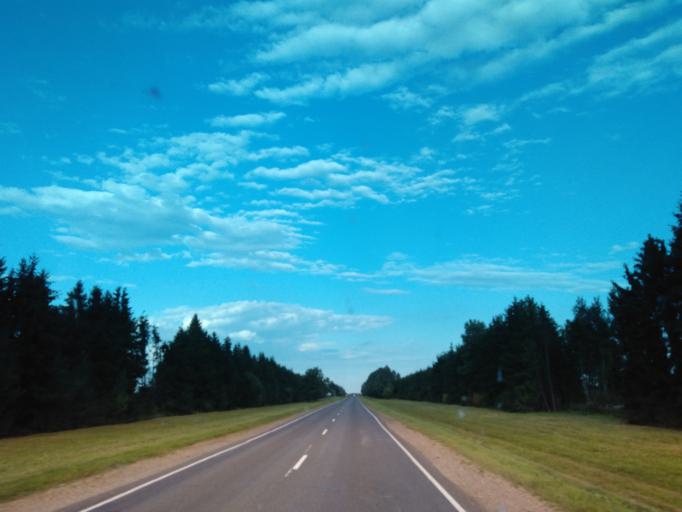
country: BY
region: Minsk
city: Uzda
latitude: 53.4385
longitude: 27.3146
